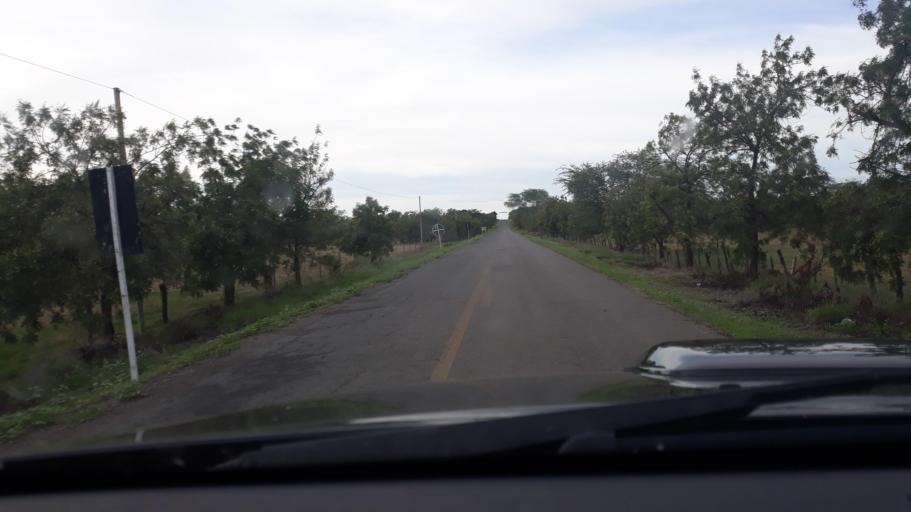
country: BR
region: Bahia
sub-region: Guanambi
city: Guanambi
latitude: -13.9186
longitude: -42.8448
